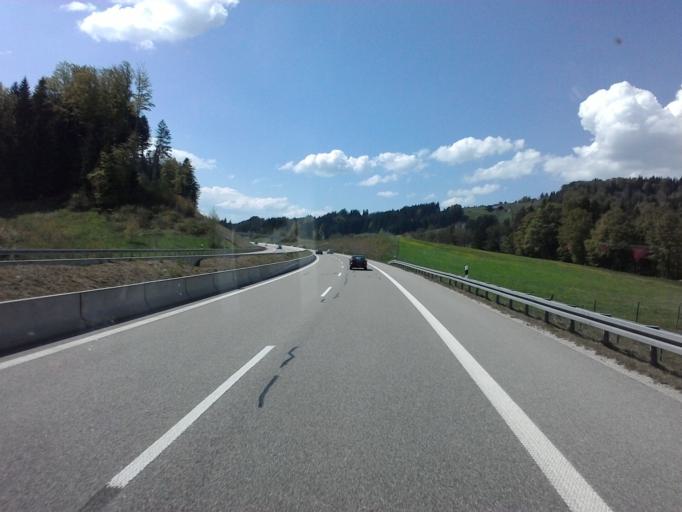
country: DE
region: Bavaria
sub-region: Swabia
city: Hopferau
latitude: 47.6261
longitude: 10.6546
